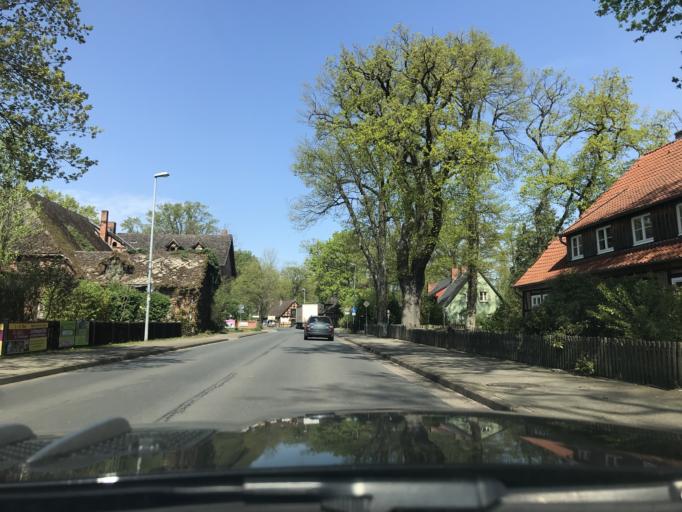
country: DE
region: Lower Saxony
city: Eickeloh
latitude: 52.7274
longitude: 9.6097
